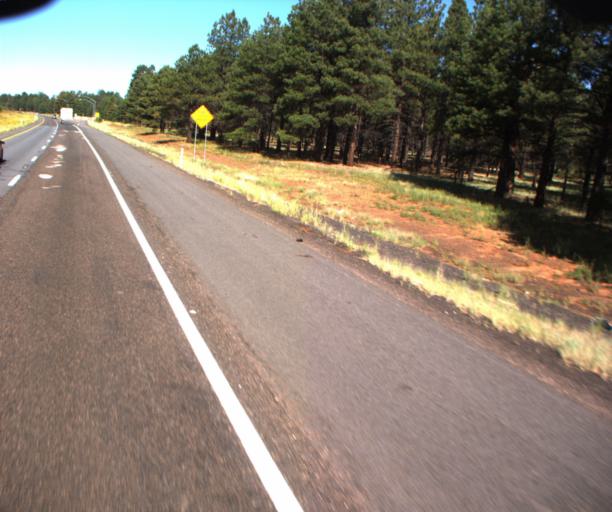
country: US
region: Arizona
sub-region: Coconino County
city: Parks
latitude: 35.2496
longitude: -111.8614
